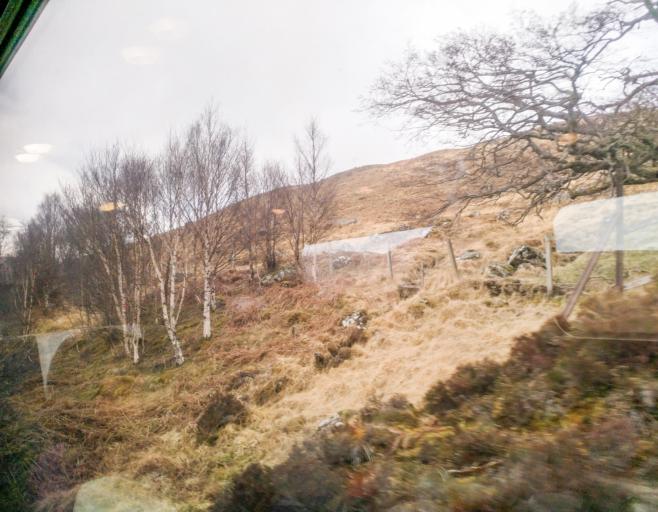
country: GB
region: Scotland
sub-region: Highland
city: Spean Bridge
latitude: 56.7768
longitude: -4.7304
